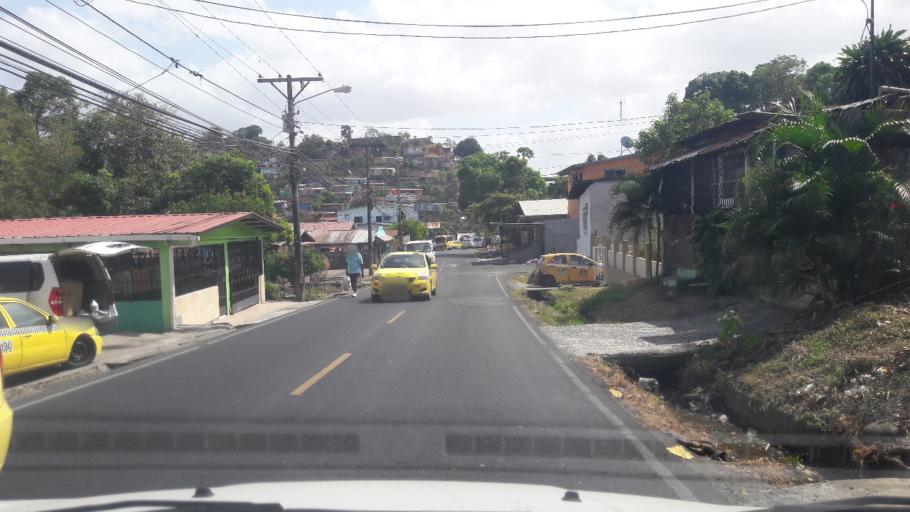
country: PA
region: Panama
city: San Miguelito
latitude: 9.0468
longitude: -79.4976
